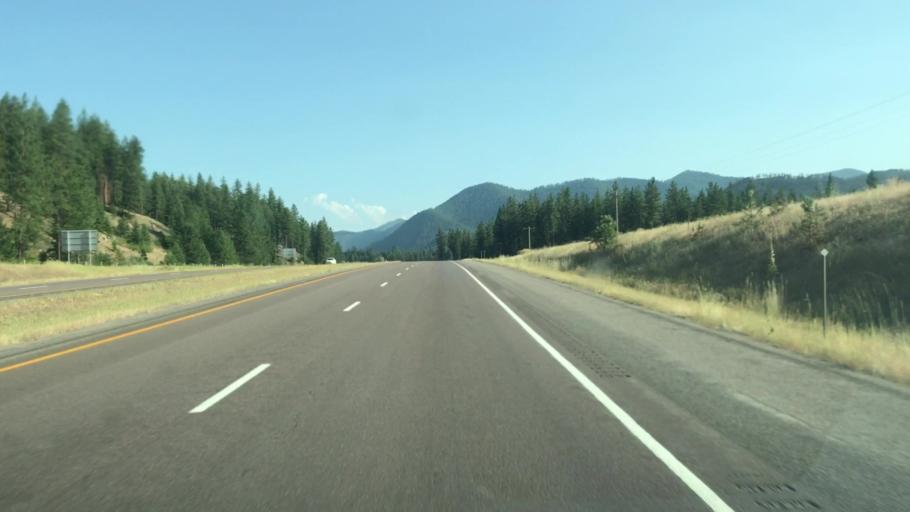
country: US
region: Montana
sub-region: Mineral County
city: Superior
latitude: 47.0638
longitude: -114.7638
